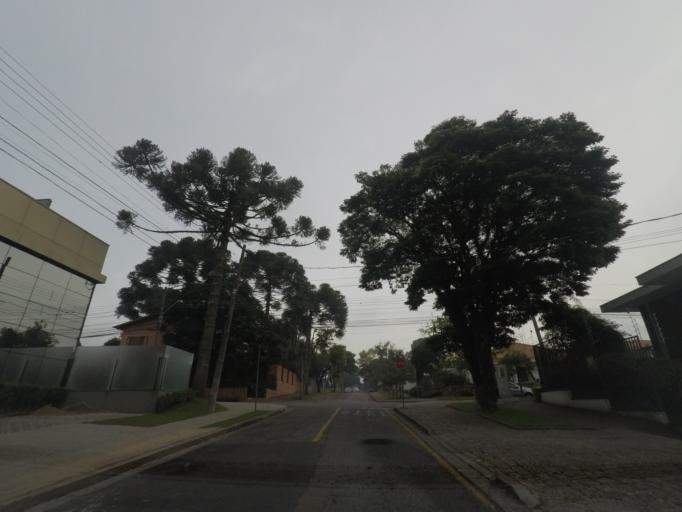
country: BR
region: Parana
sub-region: Curitiba
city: Curitiba
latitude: -25.4416
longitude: -49.2914
